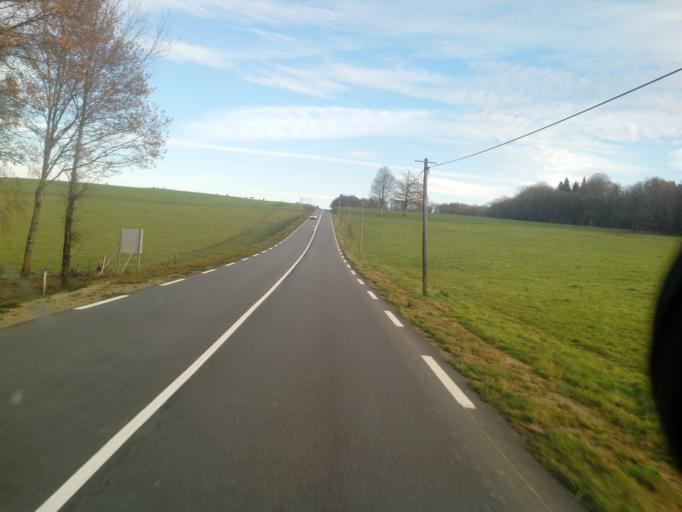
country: FR
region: Limousin
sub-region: Departement de la Haute-Vienne
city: Neuvic-Entier
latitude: 45.7304
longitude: 1.6335
